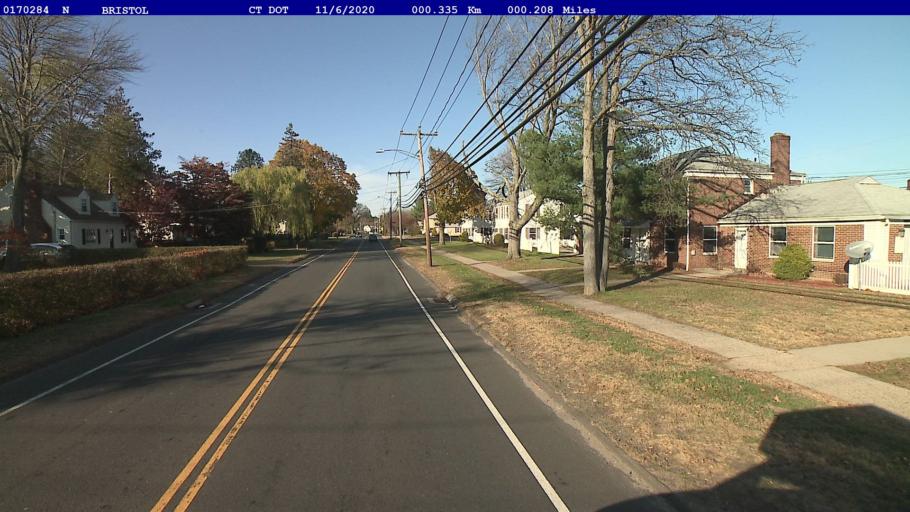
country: US
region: Connecticut
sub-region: Hartford County
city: Bristol
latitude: 41.6926
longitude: -72.9279
